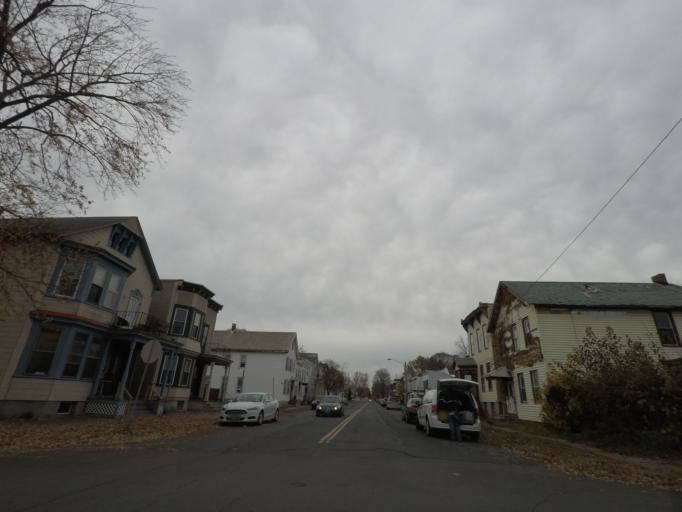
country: US
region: New York
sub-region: Saratoga County
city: Waterford
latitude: 42.7780
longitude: -73.6744
